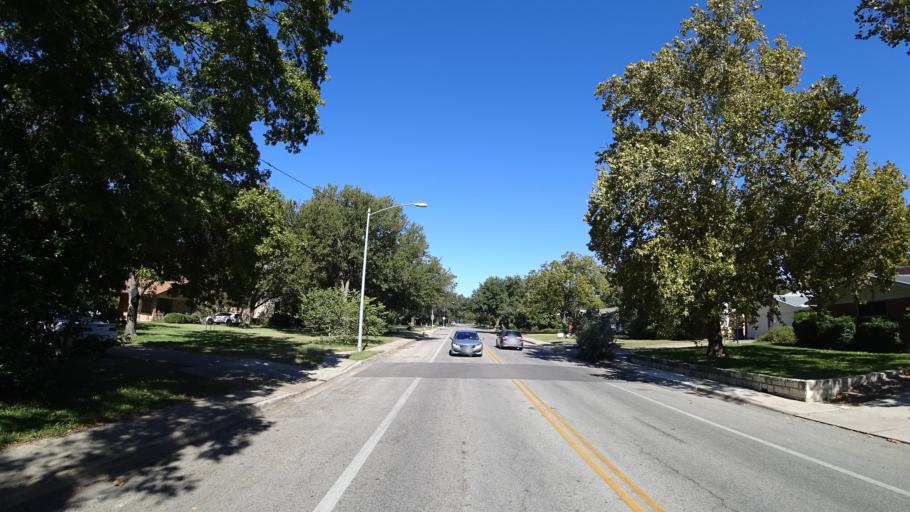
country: US
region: Texas
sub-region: Travis County
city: Austin
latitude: 30.3270
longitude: -97.7453
